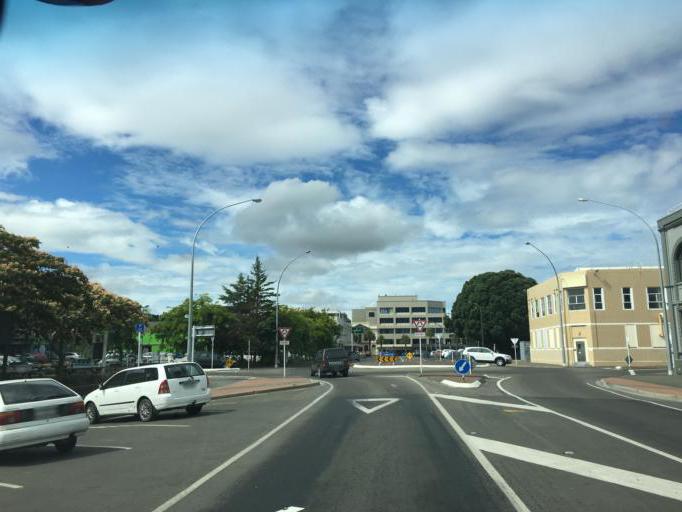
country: NZ
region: Gisborne
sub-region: Gisborne District
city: Gisborne
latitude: -38.6694
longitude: 178.0264
